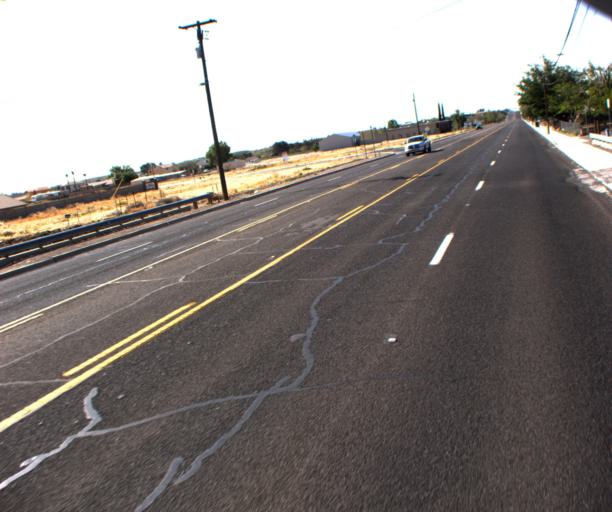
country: US
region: Arizona
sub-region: Graham County
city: Safford
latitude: 32.8141
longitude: -109.7077
